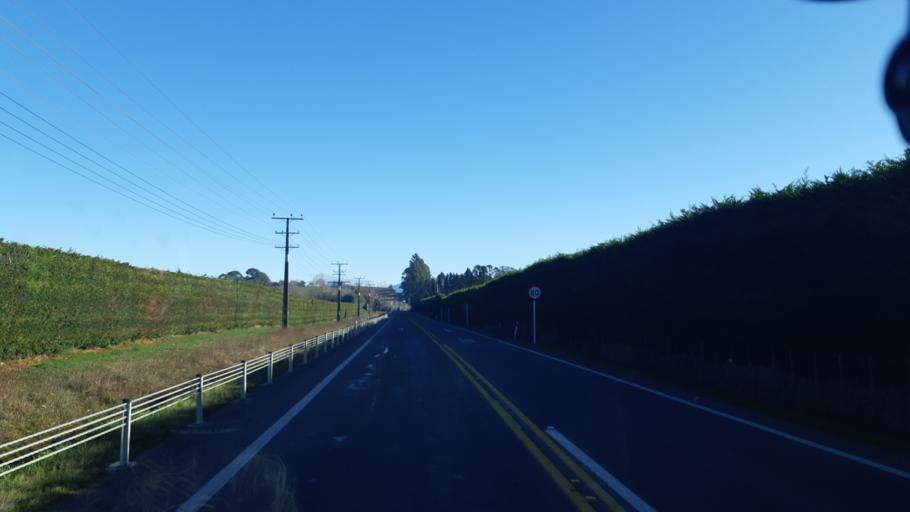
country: NZ
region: Tasman
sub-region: Tasman District
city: Mapua
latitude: -41.3018
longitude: 173.1123
